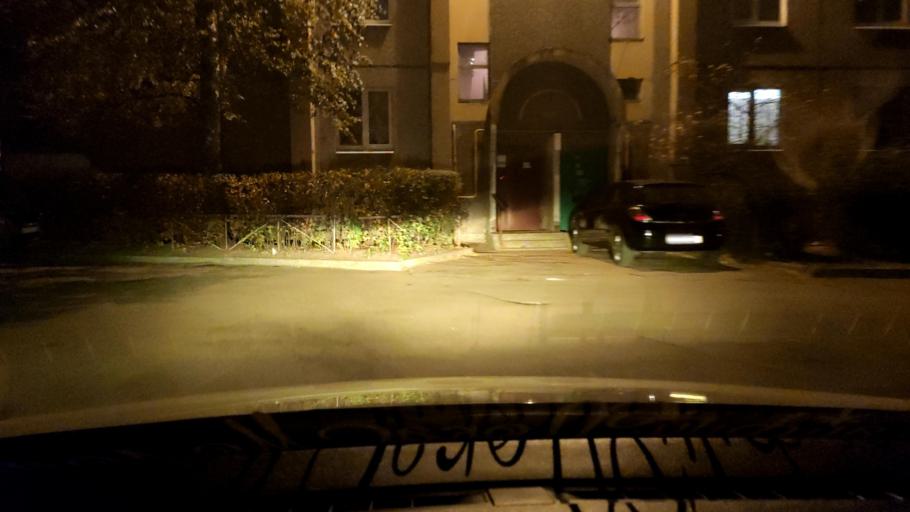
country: RU
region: Voronezj
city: Pridonskoy
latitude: 51.6559
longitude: 39.1257
